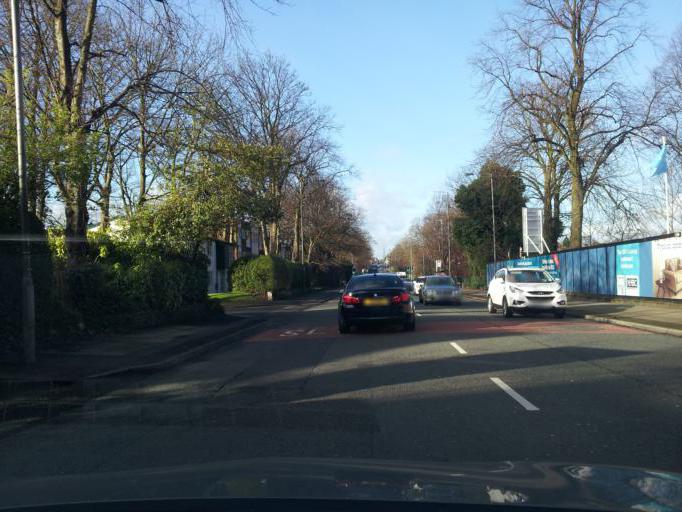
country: GB
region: England
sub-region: Borough of Bury
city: Prestwich
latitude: 53.5264
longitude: -2.2792
